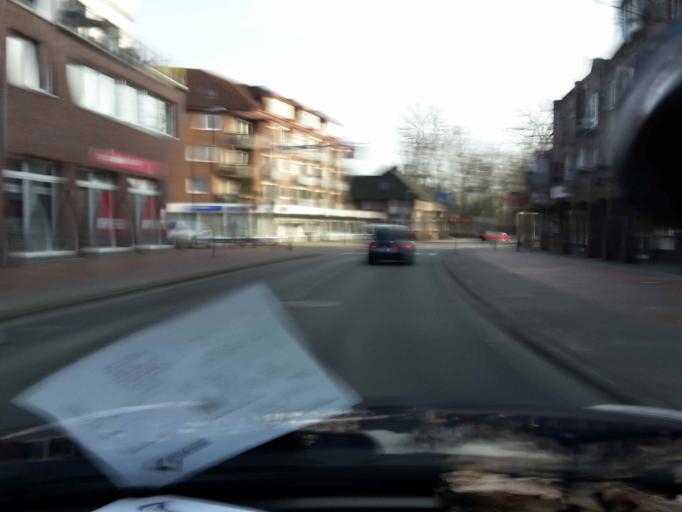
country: DE
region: Lower Saxony
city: Buchholz in der Nordheide
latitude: 53.3282
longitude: 9.8826
